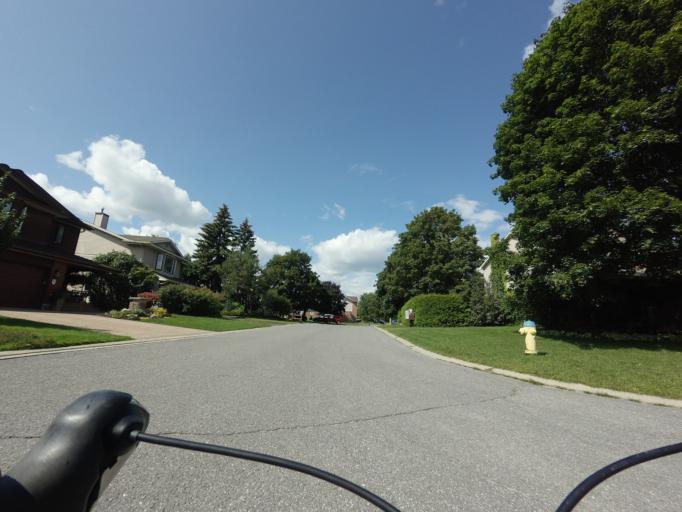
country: CA
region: Ontario
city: Bells Corners
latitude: 45.2906
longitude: -75.8685
